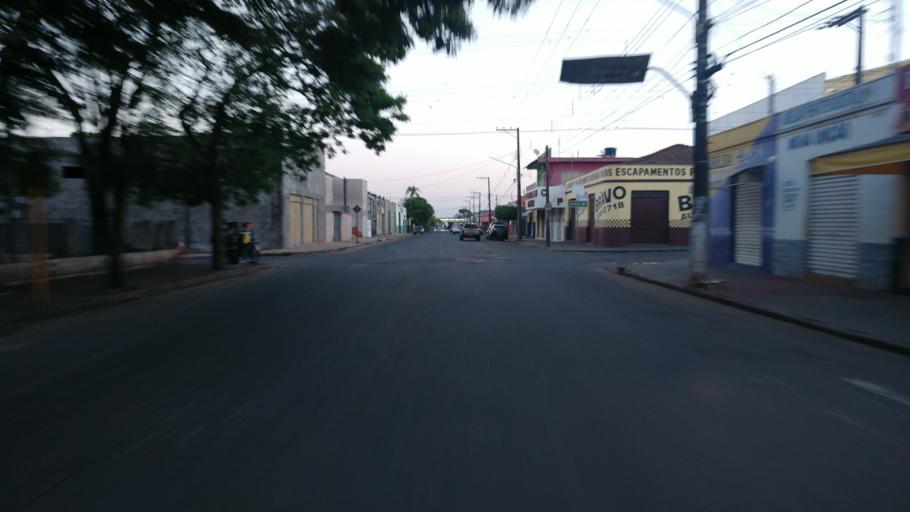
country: BR
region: Sao Paulo
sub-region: Paraguacu Paulista
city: Paraguacu Paulista
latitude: -22.4099
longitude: -50.5706
